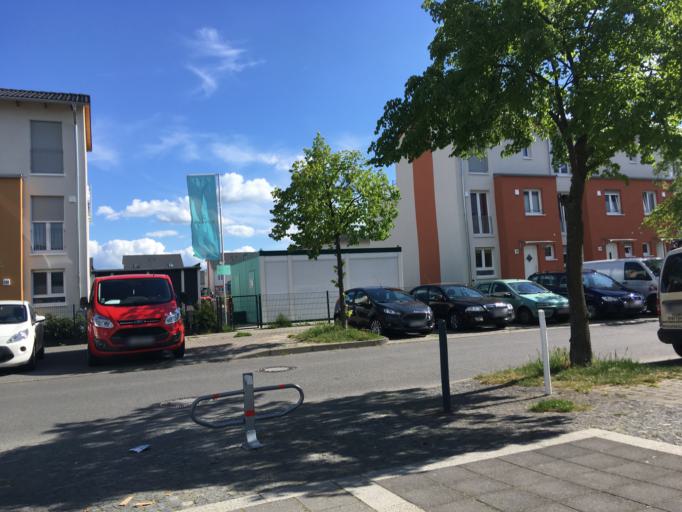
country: DE
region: Brandenburg
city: Bernau bei Berlin
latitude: 52.6711
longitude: 13.5536
